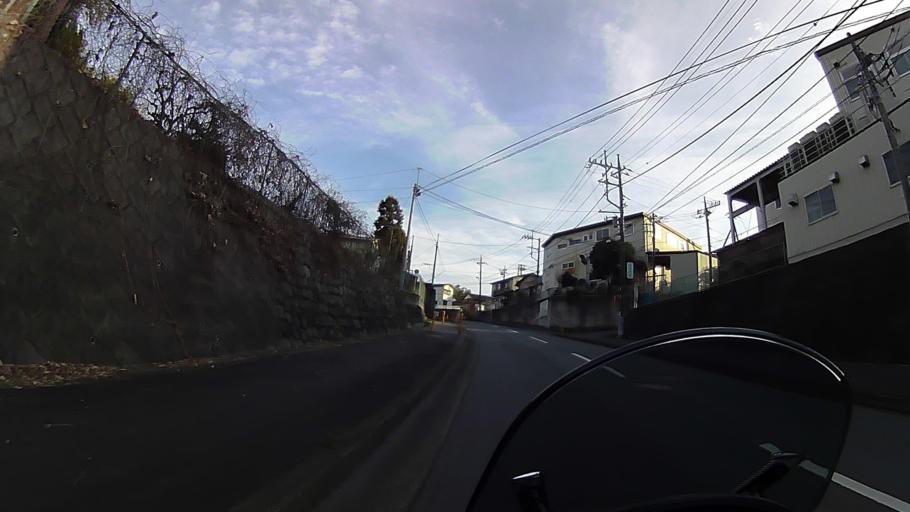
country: JP
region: Kanagawa
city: Atsugi
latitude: 35.4295
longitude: 139.4196
